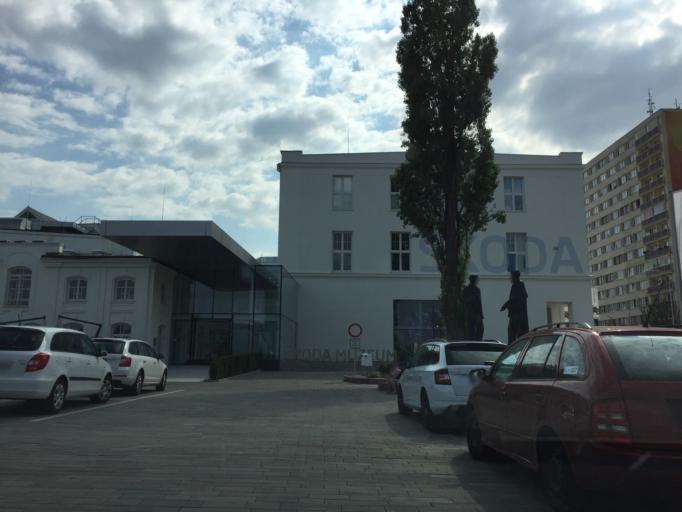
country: CZ
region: Central Bohemia
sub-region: Okres Mlada Boleslav
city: Mlada Boleslav
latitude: 50.4192
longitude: 14.9141
